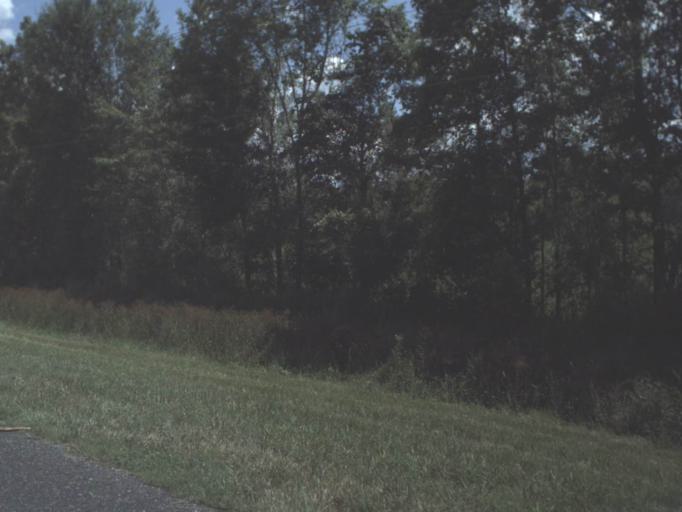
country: US
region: Florida
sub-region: Taylor County
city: Steinhatchee
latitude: 29.8701
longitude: -83.3980
